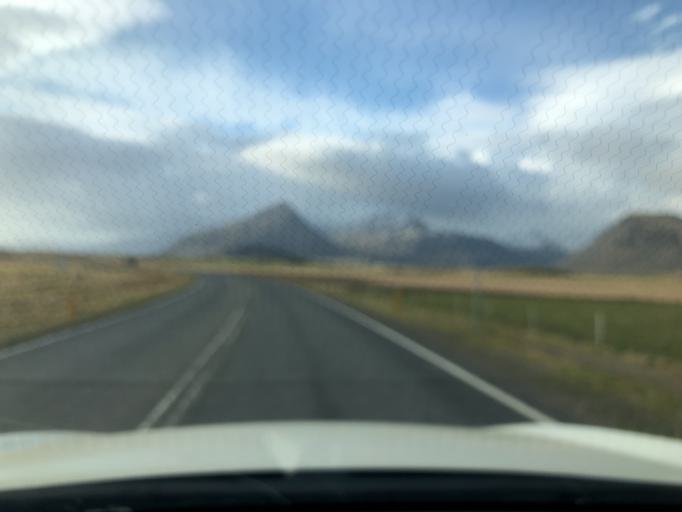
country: IS
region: East
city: Hoefn
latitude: 64.2903
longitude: -15.1823
